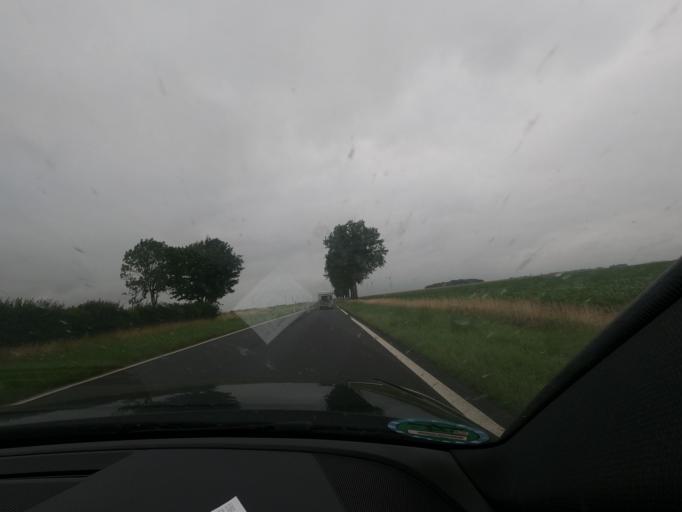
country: FR
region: Picardie
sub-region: Departement de la Somme
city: Rosieres-en-Santerre
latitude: 49.7388
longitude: 2.6912
